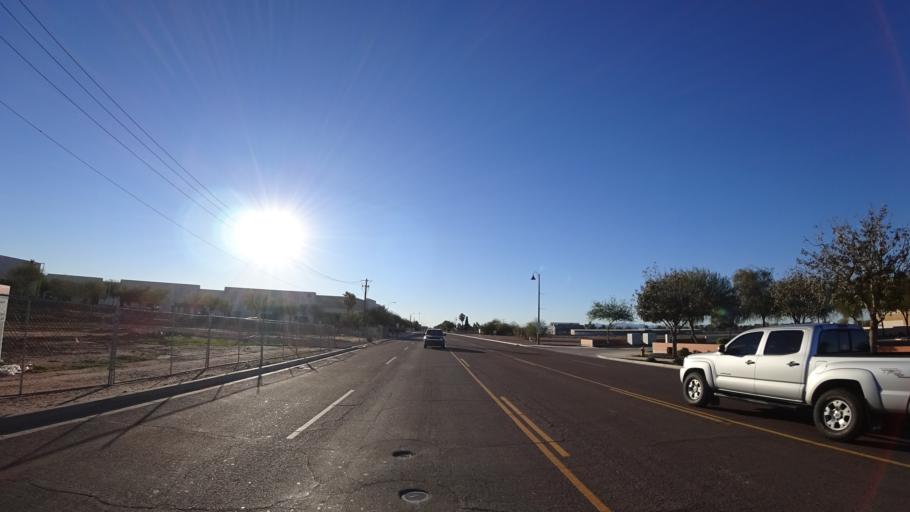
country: US
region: Arizona
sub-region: Maricopa County
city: Tolleson
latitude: 33.4516
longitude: -112.2404
